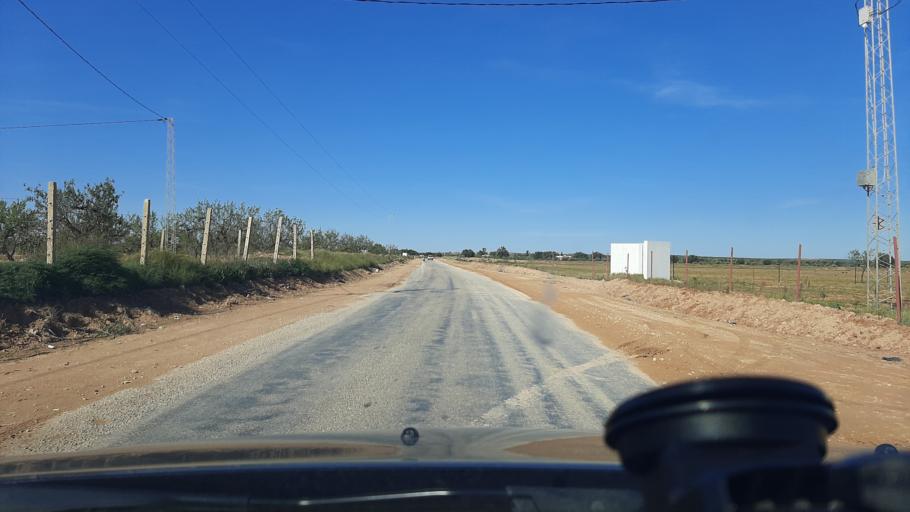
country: TN
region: Safaqis
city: Sfax
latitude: 34.9164
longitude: 10.5842
